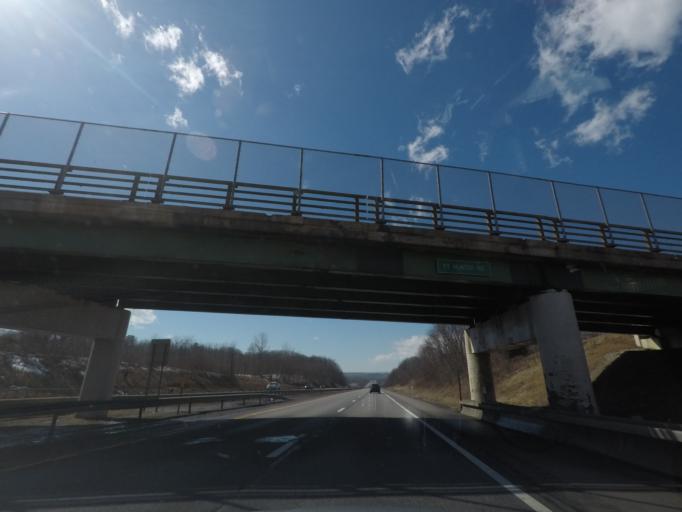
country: US
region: New York
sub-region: Montgomery County
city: Tribes Hill
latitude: 42.9321
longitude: -74.2709
